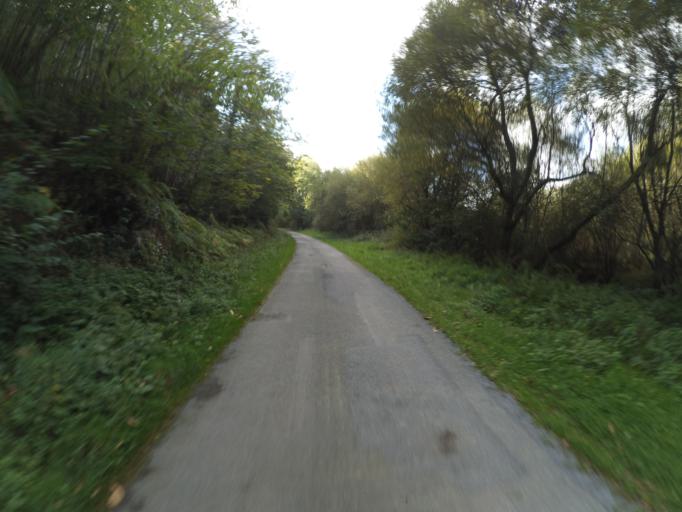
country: FR
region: Brittany
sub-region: Departement du Morbihan
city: Peillac
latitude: 47.7259
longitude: -2.2166
